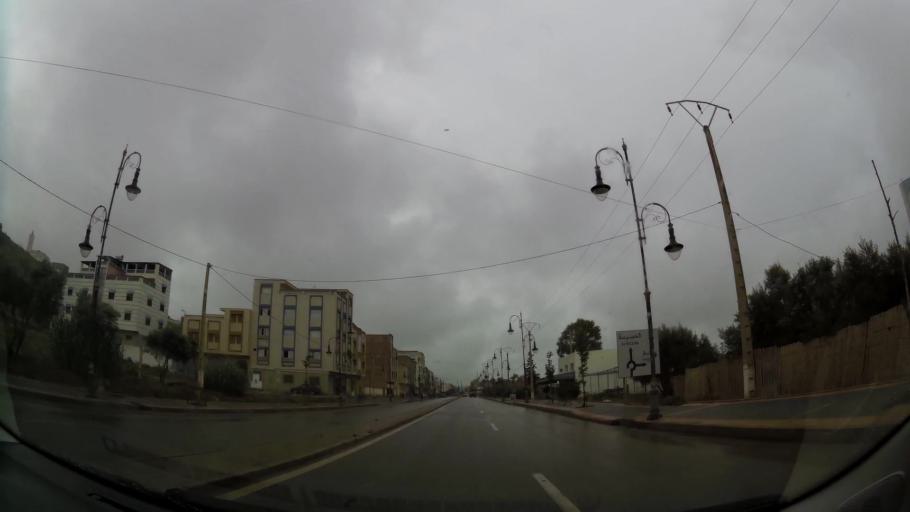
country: MA
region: Taza-Al Hoceima-Taounate
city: Imzourene
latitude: 35.1701
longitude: -3.8603
